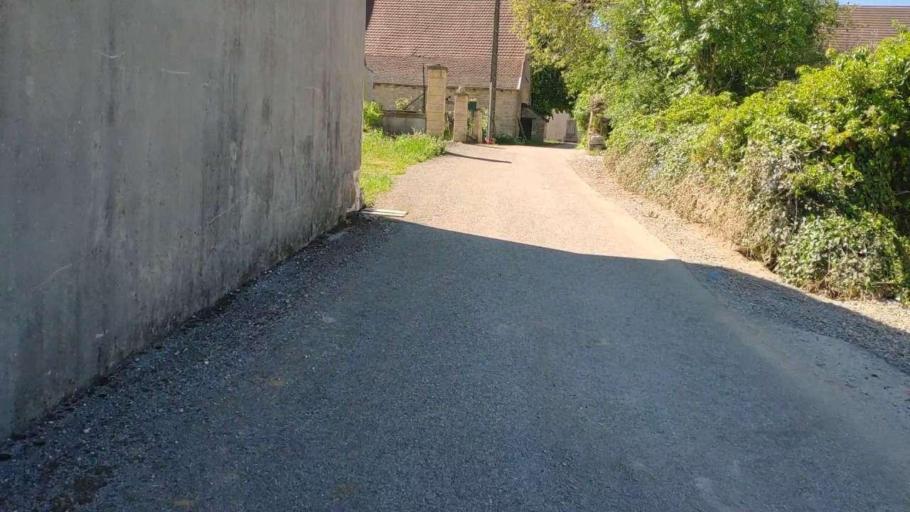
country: FR
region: Franche-Comte
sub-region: Departement du Jura
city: Clairvaux-les-Lacs
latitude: 46.6973
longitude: 5.7248
